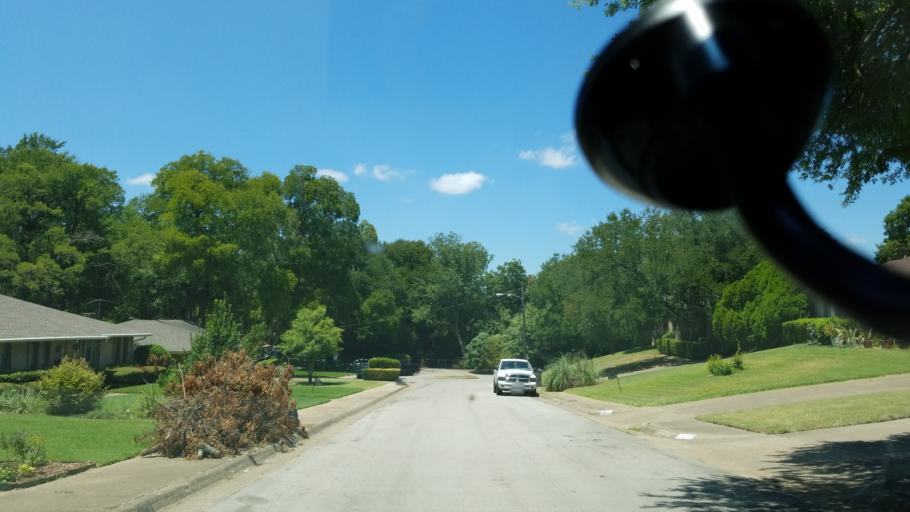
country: US
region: Texas
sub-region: Dallas County
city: Cockrell Hill
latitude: 32.6799
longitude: -96.8200
